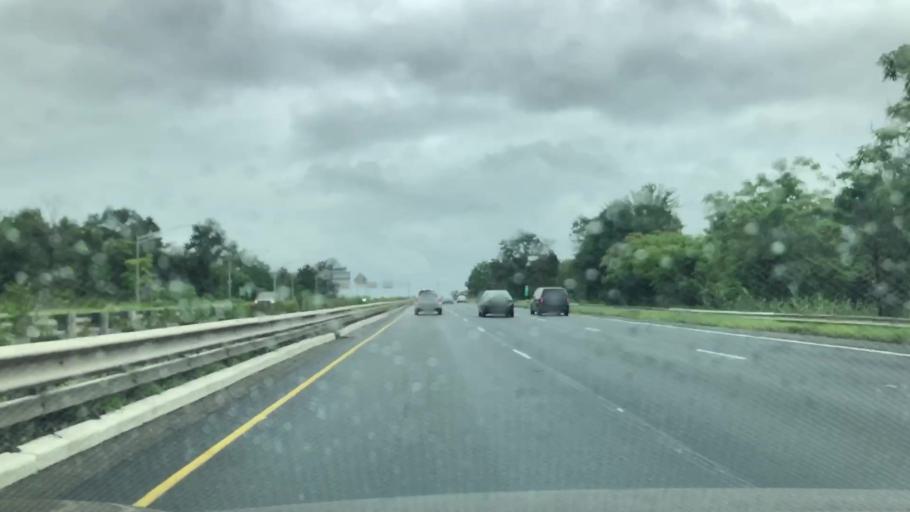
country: US
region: New Jersey
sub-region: Middlesex County
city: Fords
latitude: 40.5275
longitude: -74.3322
